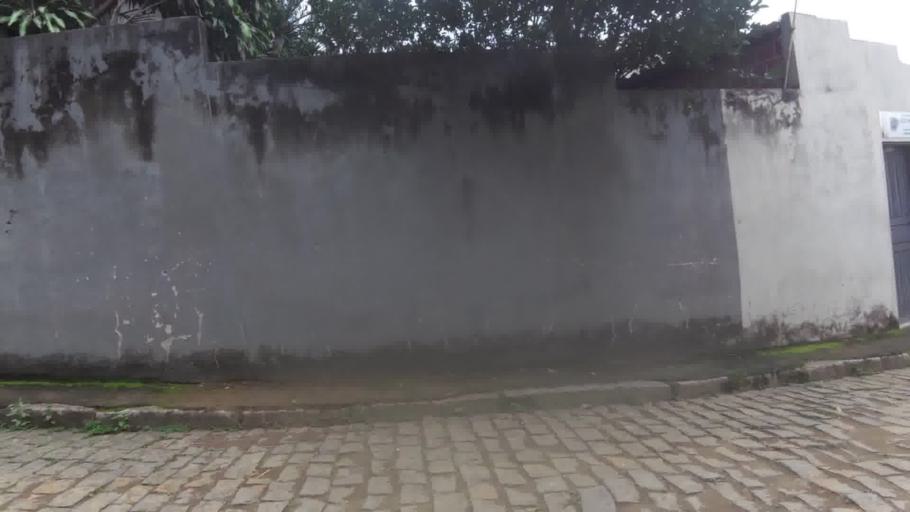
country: BR
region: Espirito Santo
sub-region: Iconha
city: Iconha
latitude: -20.7923
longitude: -40.8134
